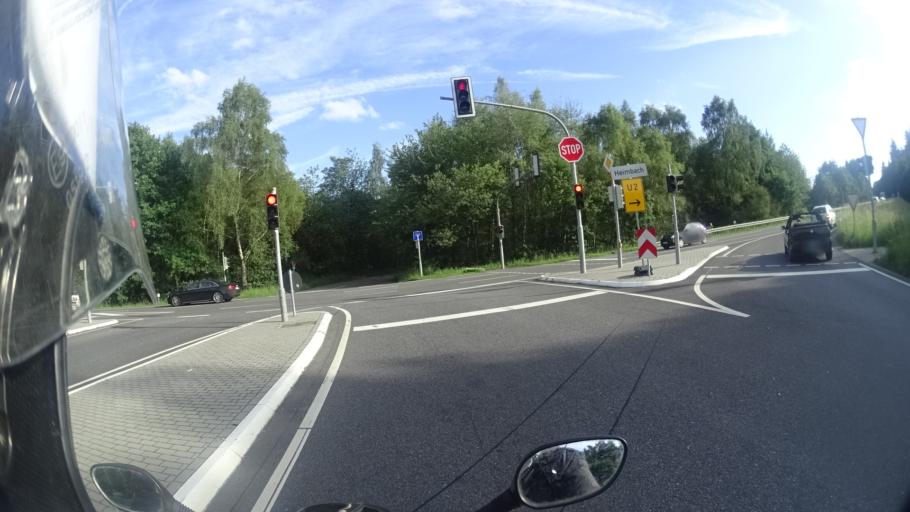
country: DE
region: Hesse
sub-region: Regierungsbezirk Darmstadt
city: Bad Schwalbach
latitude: 50.1189
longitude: 8.0807
